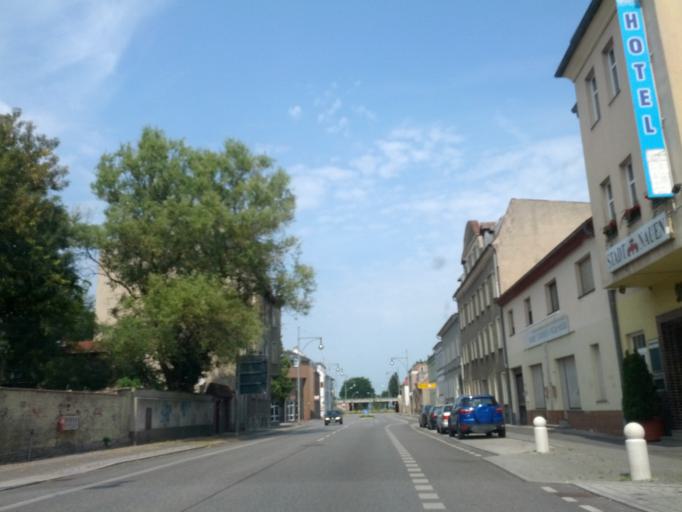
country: DE
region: Brandenburg
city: Nauen
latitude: 52.6108
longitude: 12.8812
